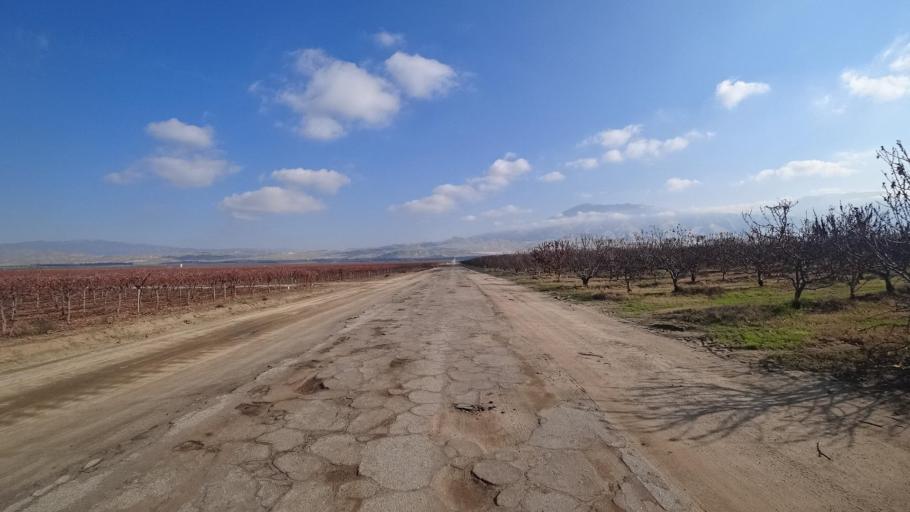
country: US
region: California
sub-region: Kern County
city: Arvin
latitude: 35.2530
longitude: -118.7868
